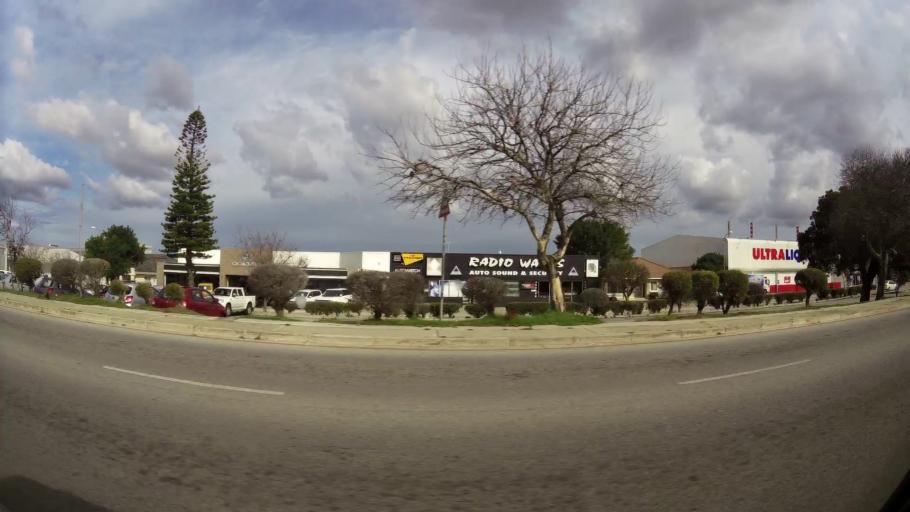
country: ZA
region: Eastern Cape
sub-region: Nelson Mandela Bay Metropolitan Municipality
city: Port Elizabeth
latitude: -33.9480
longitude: 25.5565
